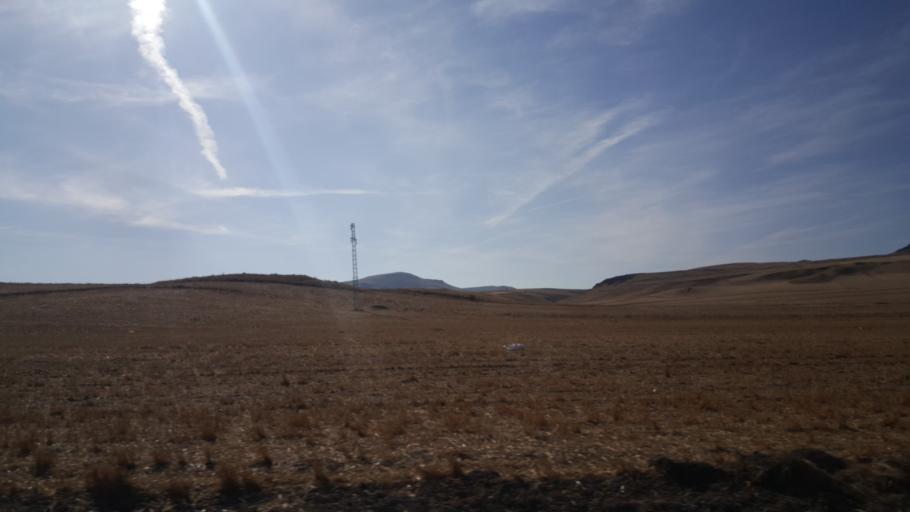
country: TR
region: Ankara
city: Yenice
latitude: 39.3313
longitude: 32.7518
